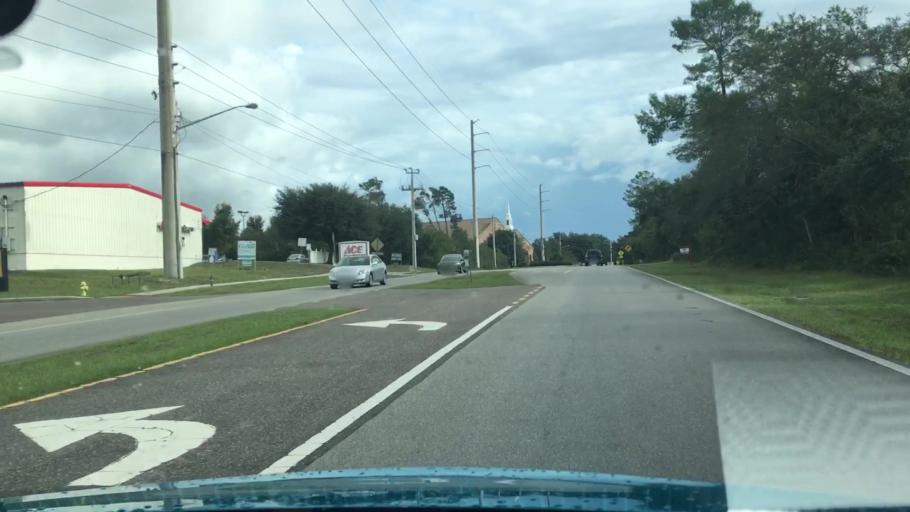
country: US
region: Florida
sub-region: Volusia County
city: Lake Helen
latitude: 28.9288
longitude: -81.1874
